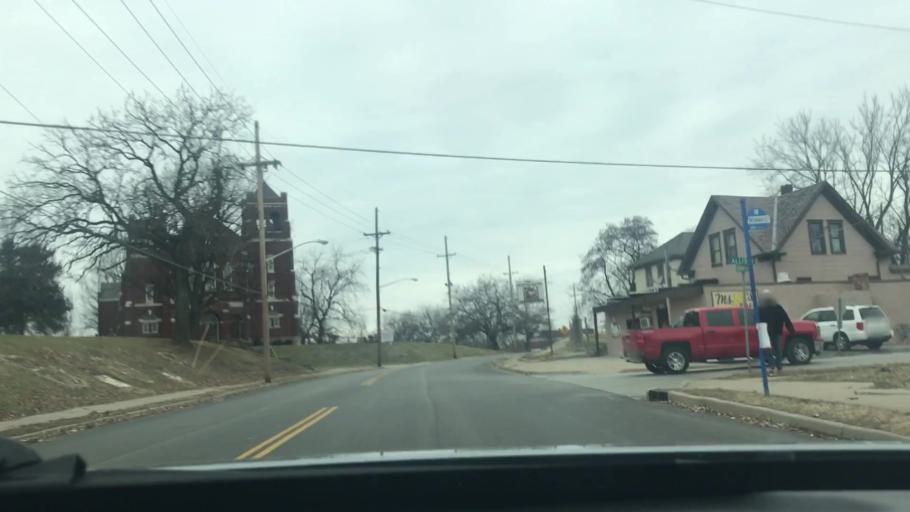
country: US
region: Kansas
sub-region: Wyandotte County
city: Kansas City
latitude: 39.1322
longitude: -94.6281
